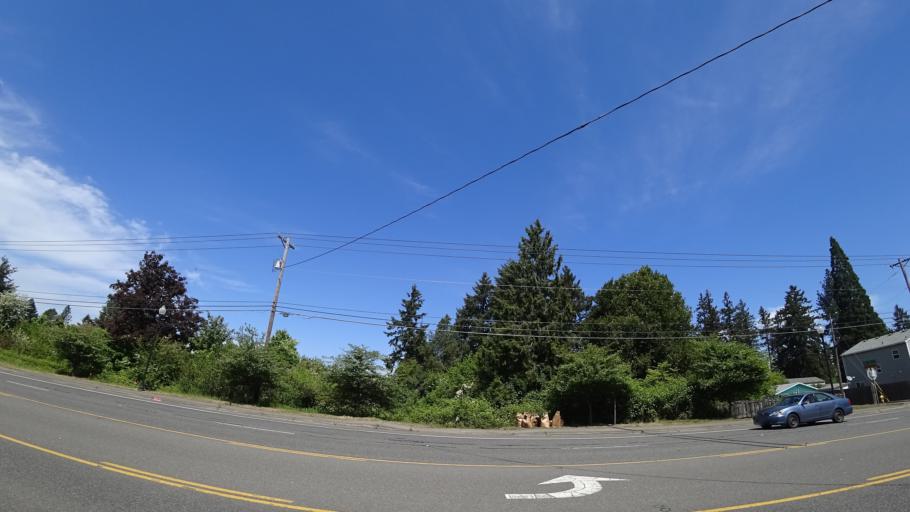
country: US
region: Oregon
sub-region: Washington County
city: Aloha
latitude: 45.4837
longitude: -122.8440
